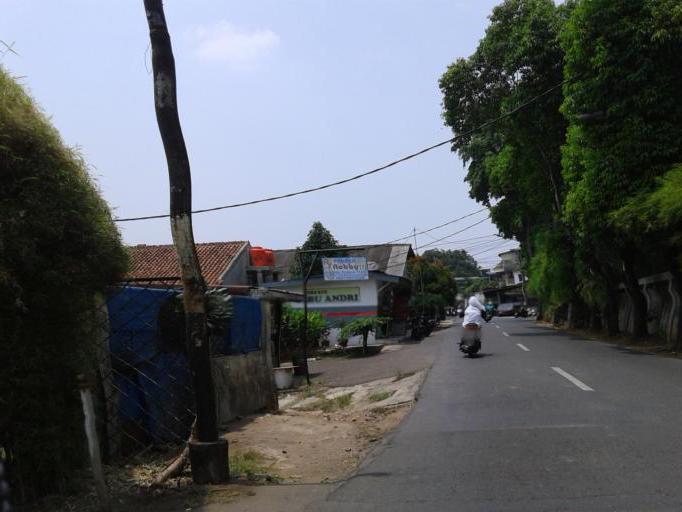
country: ID
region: West Java
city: Depok
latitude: -6.3263
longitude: 106.8162
